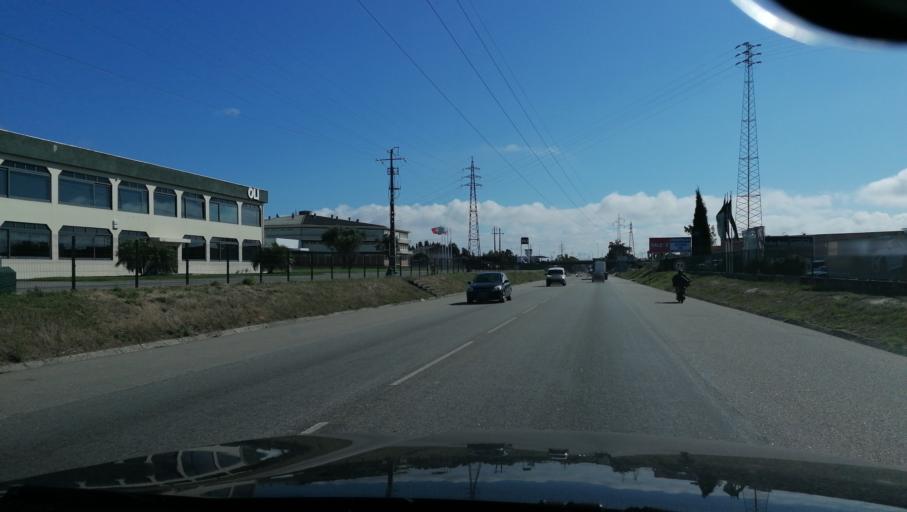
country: PT
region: Aveiro
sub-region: Aveiro
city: Aveiro
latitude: 40.6573
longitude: -8.6166
